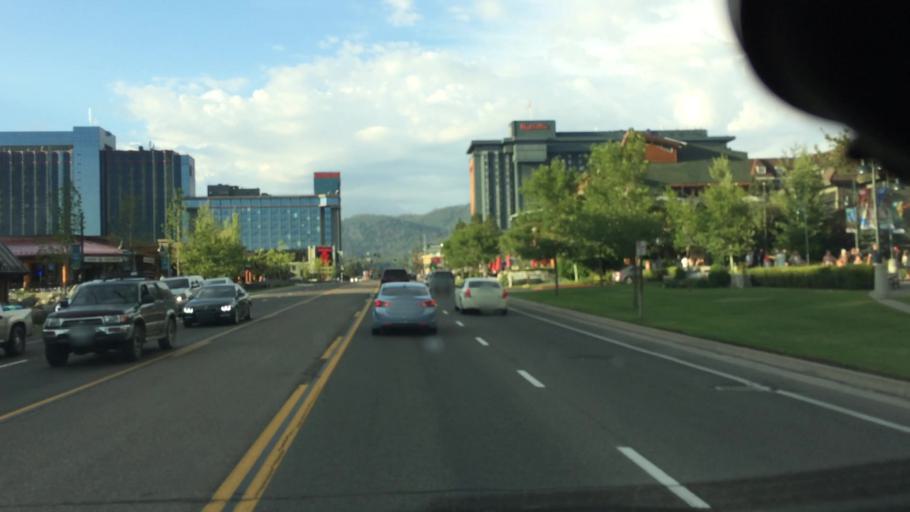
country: US
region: Nevada
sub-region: Douglas County
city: Kingsbury
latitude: 38.9571
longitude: -119.9434
